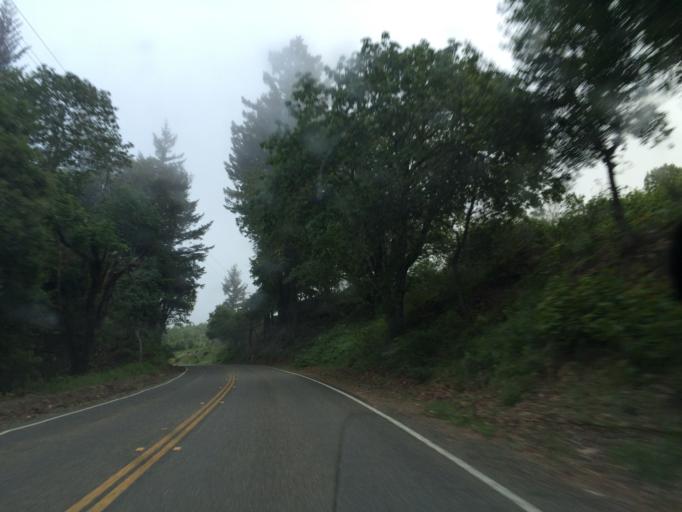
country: US
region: California
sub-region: Santa Clara County
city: Los Altos Hills
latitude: 37.3084
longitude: -122.1678
